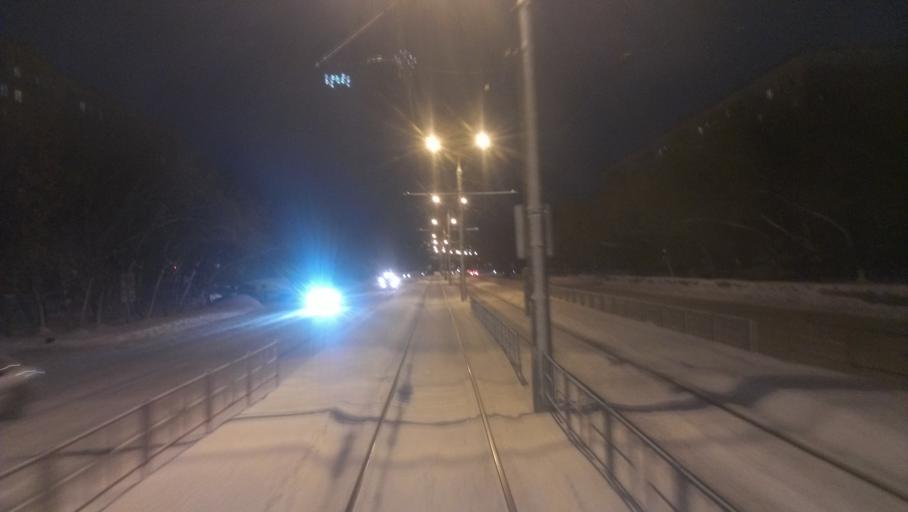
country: RU
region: Altai Krai
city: Novosilikatnyy
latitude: 53.3716
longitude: 83.6777
